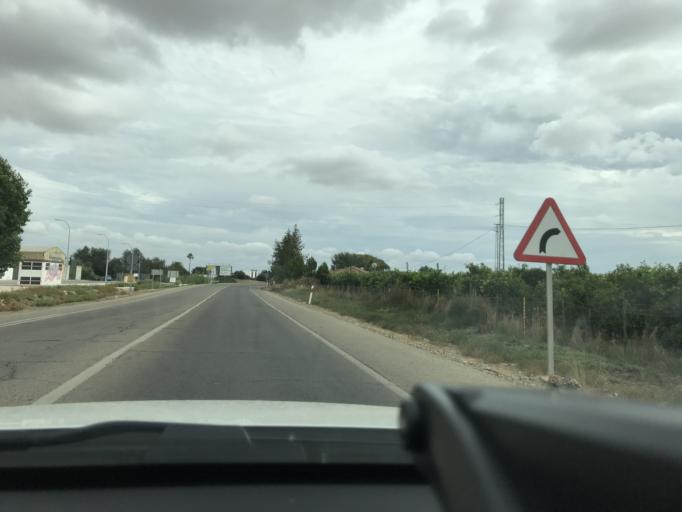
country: ES
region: Andalusia
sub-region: Provincia de Sevilla
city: La Rinconada
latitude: 37.4716
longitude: -5.9725
